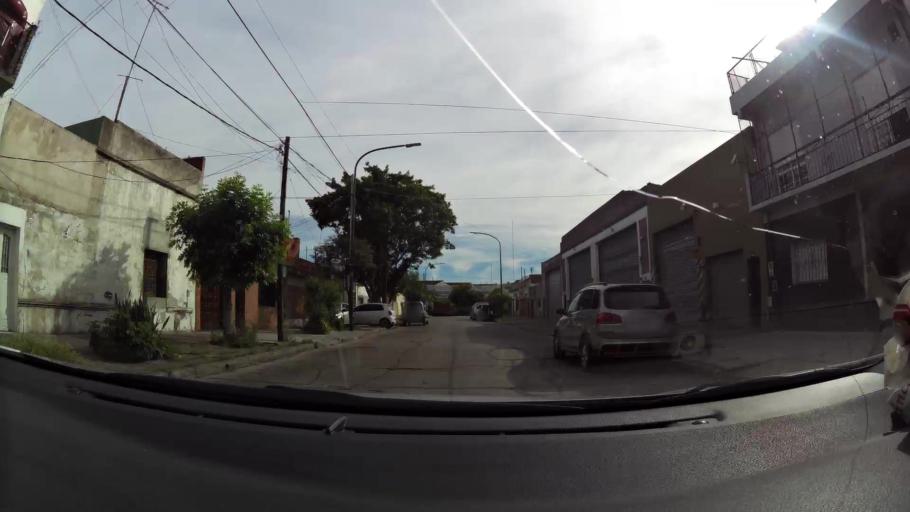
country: AR
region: Buenos Aires F.D.
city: Buenos Aires
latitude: -34.6463
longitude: -58.4225
